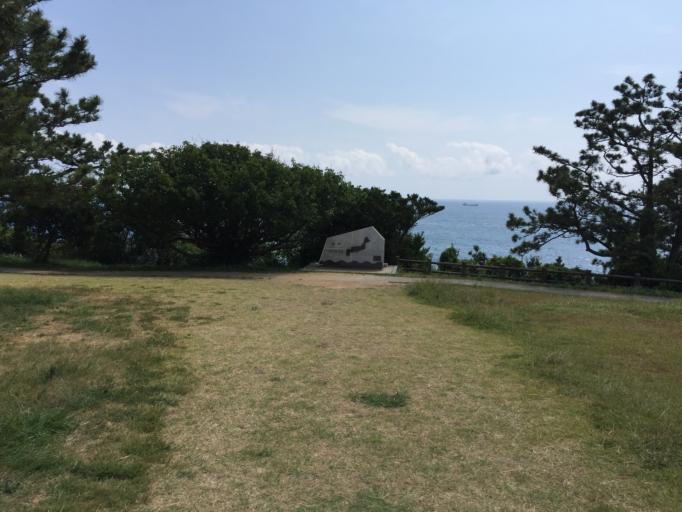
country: JP
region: Wakayama
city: Shingu
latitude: 33.4363
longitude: 135.7617
